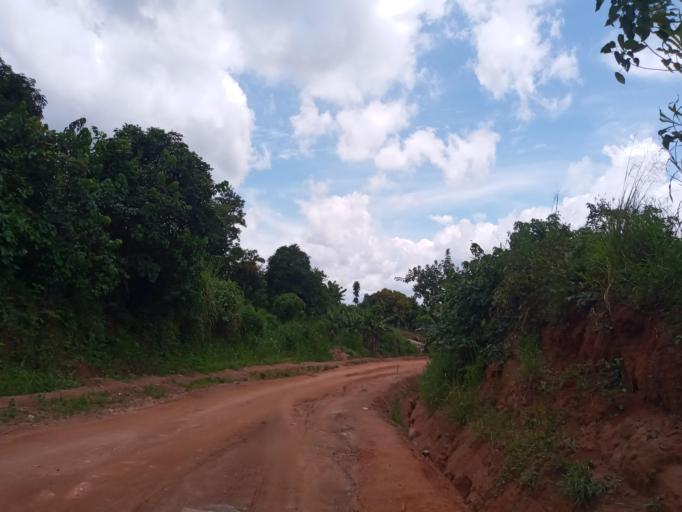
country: SL
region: Eastern Province
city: Koidu
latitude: 8.6454
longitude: -10.9244
